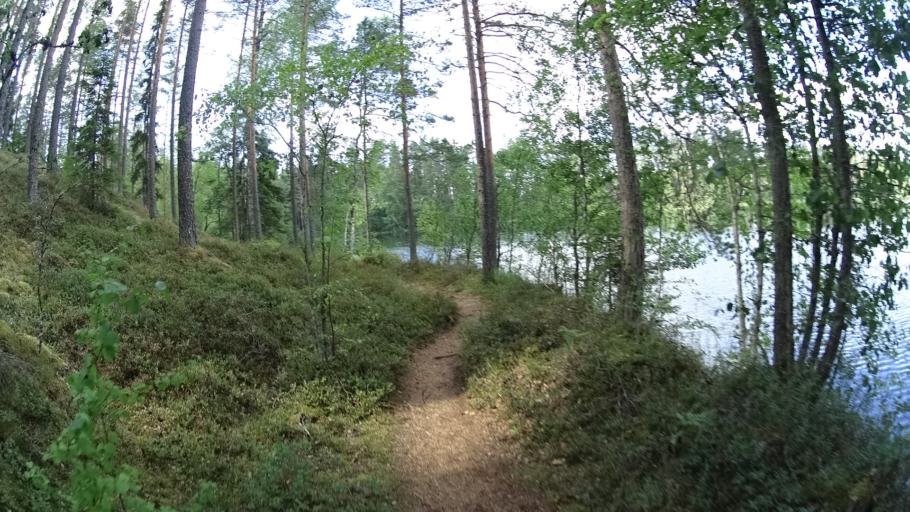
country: FI
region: Uusimaa
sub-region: Helsinki
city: Kaerkoelae
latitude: 60.7349
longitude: 24.0738
